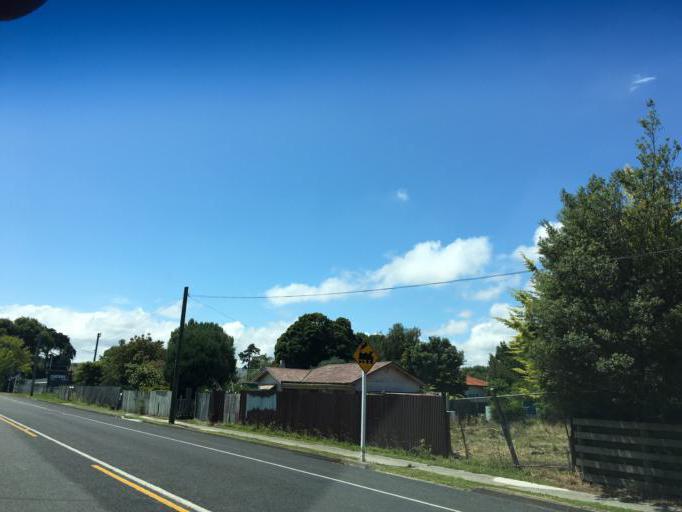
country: NZ
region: Hawke's Bay
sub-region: Wairoa District
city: Wairoa
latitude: -39.0249
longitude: 177.4175
